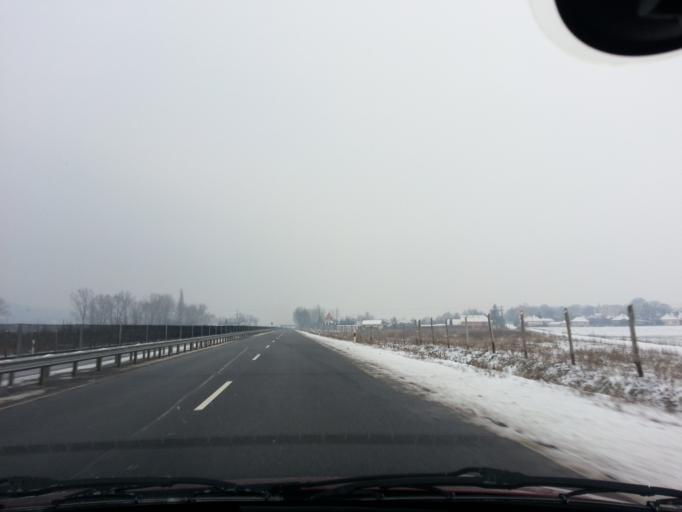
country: HU
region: Nograd
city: Jobbagyi
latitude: 47.8394
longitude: 19.6782
